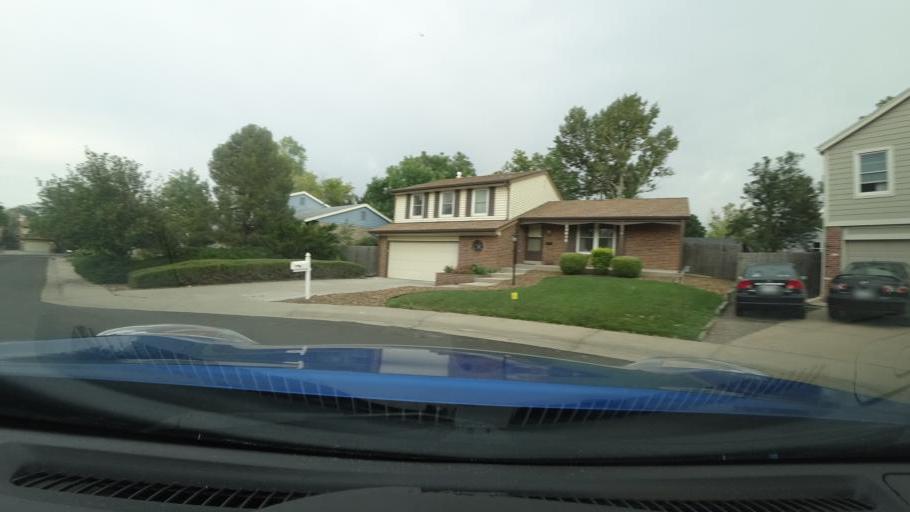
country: US
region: Colorado
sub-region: Adams County
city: Aurora
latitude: 39.6930
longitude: -104.8255
